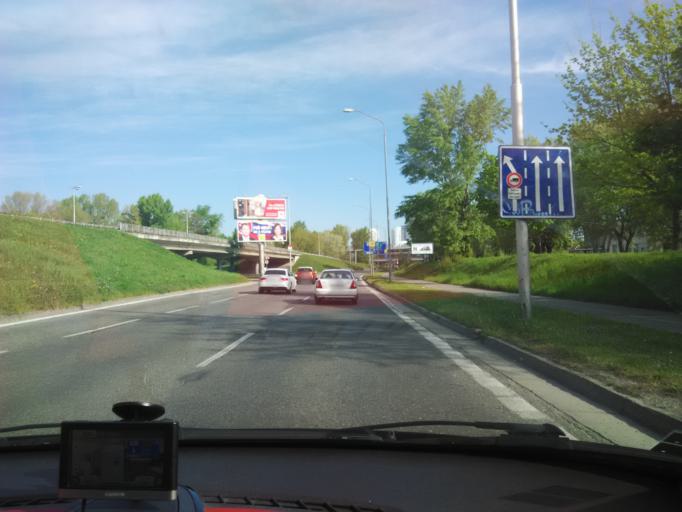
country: SK
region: Bratislavsky
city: Bratislava
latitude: 48.1267
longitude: 17.1307
